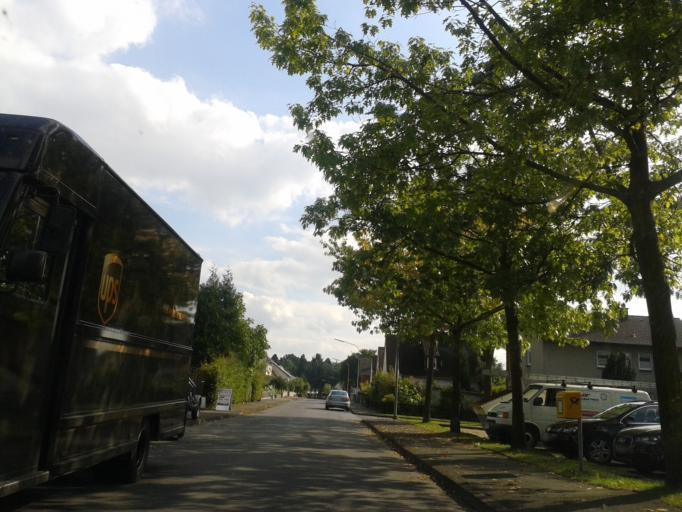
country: DE
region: North Rhine-Westphalia
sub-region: Regierungsbezirk Detmold
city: Schlangen
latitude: 51.8026
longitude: 8.8313
